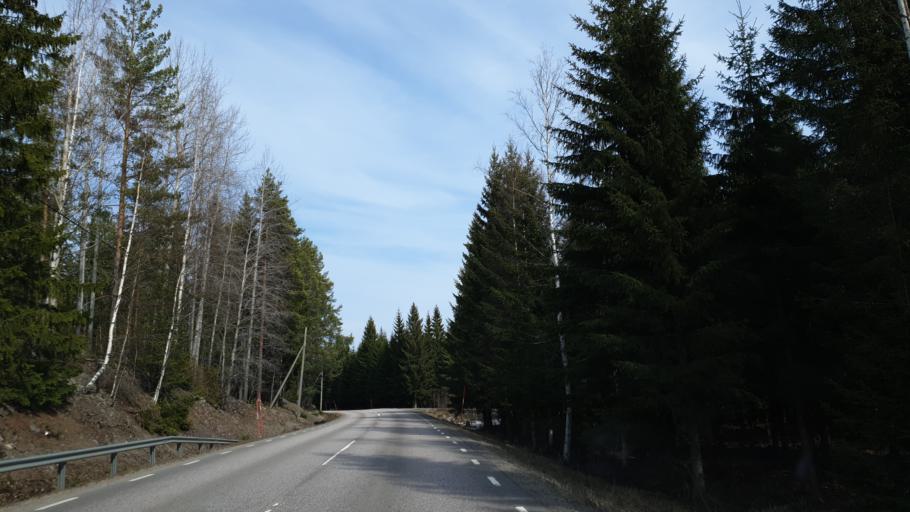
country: SE
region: Gaevleborg
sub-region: Gavle Kommun
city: Norrsundet
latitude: 60.9681
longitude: 17.0499
